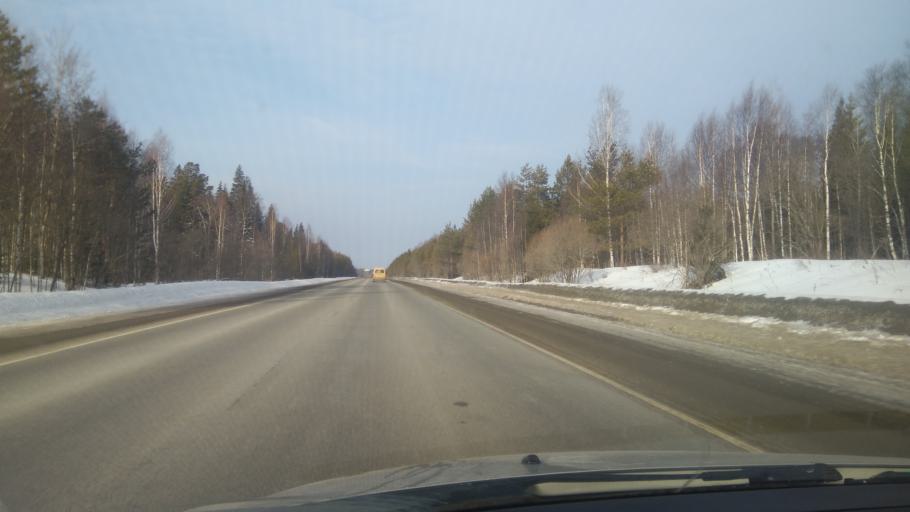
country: RU
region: Sverdlovsk
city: Nizhniye Sergi
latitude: 56.8241
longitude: 59.2889
